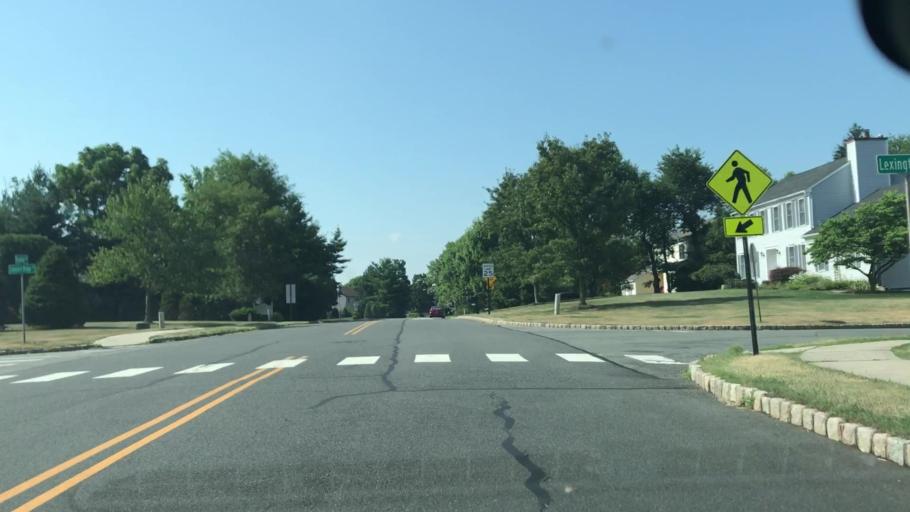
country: US
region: New Jersey
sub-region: Hunterdon County
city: Flemington
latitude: 40.5000
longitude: -74.8447
